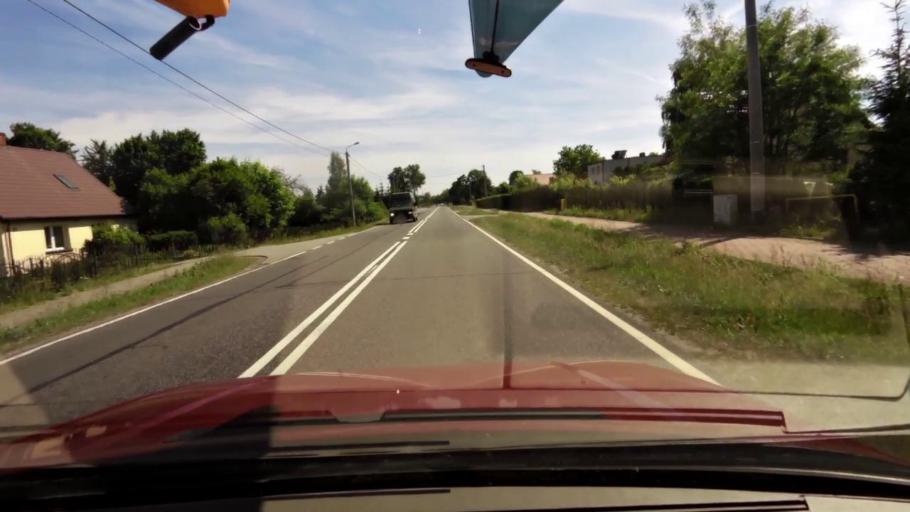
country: PL
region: Pomeranian Voivodeship
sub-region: Powiat slupski
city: Kobylnica
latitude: 54.4148
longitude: 17.0077
